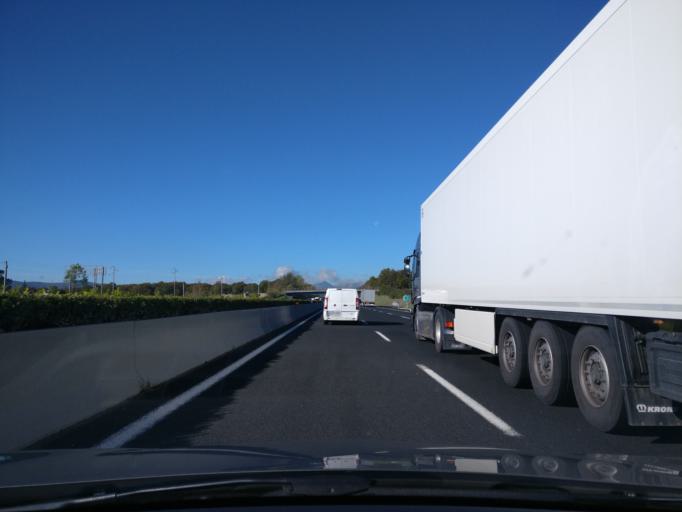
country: IT
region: Latium
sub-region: Provincia di Frosinone
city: Ceprano
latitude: 41.5461
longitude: 13.4800
